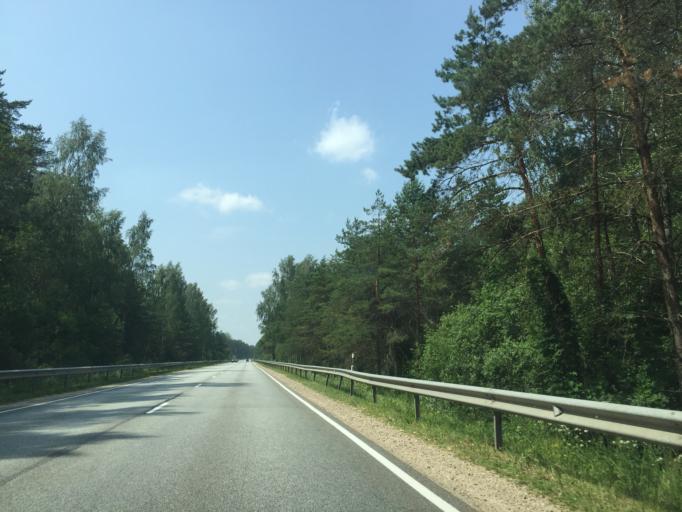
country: LV
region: Kekava
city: Kekava
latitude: 56.8101
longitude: 24.2116
